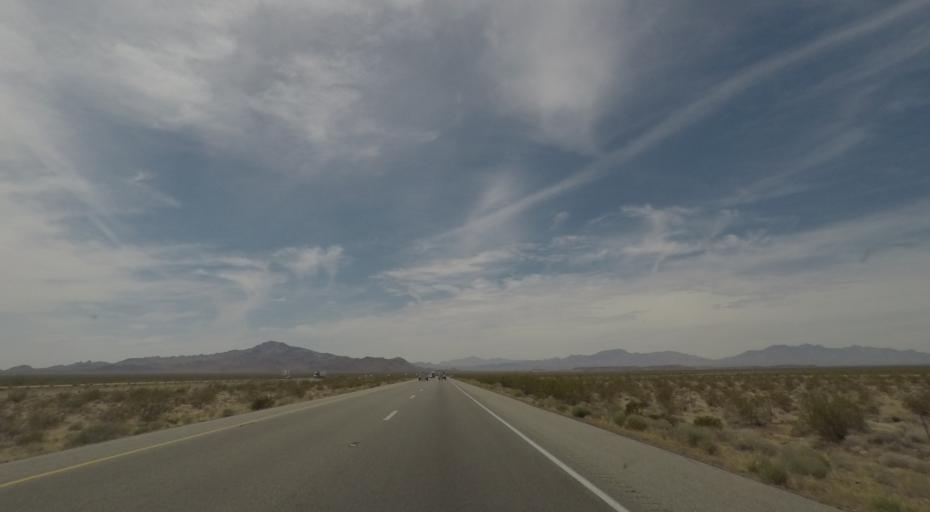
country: US
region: California
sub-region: San Bernardino County
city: Needles
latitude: 34.8080
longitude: -115.2386
